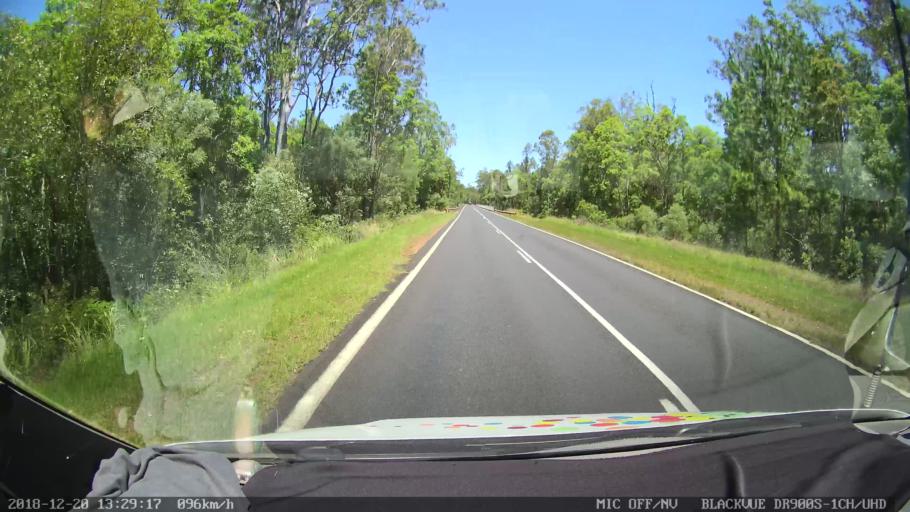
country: AU
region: New South Wales
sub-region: Clarence Valley
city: Gordon
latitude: -29.1870
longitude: 152.9890
